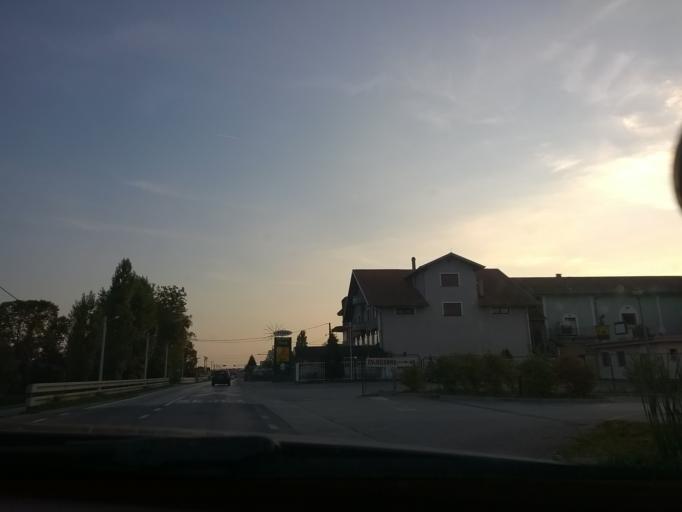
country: HR
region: Grad Zagreb
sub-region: Sesvete
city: Sesvete
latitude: 45.8654
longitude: 16.1552
